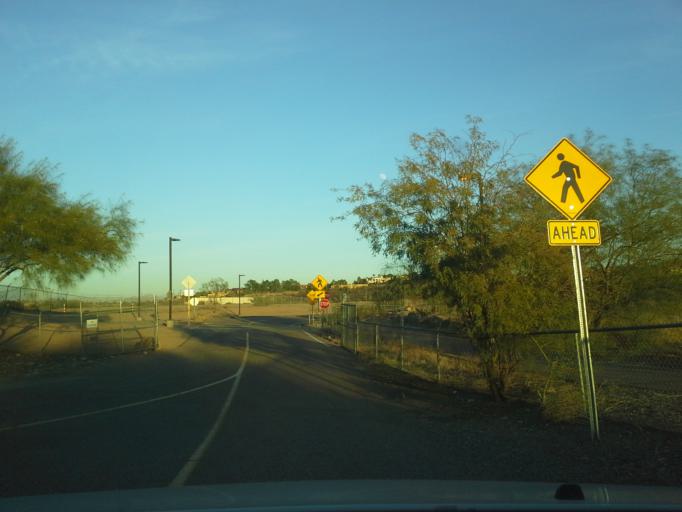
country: US
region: Arizona
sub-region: Maricopa County
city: Glendale
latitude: 33.6213
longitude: -112.1033
